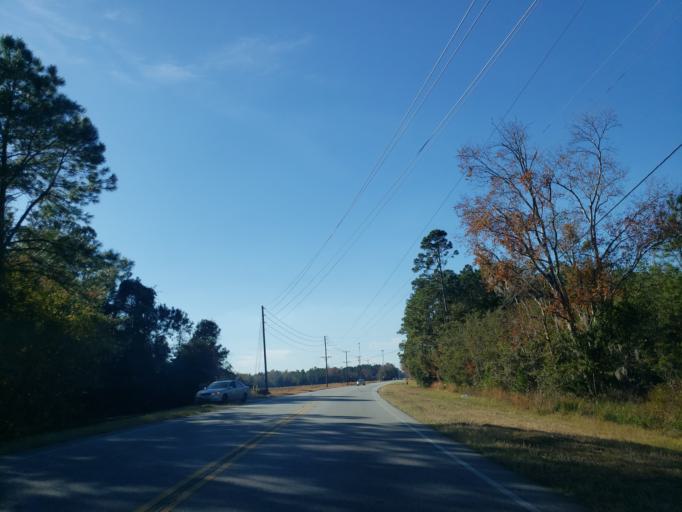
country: US
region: Georgia
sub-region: Glynn County
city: Dock Junction
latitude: 31.2726
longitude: -81.5386
